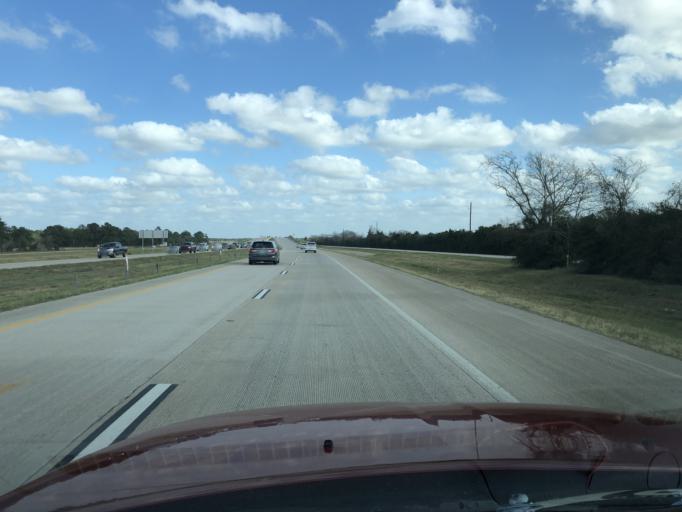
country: US
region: Texas
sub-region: Harris County
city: Cypress
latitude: 30.0499
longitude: -95.6861
